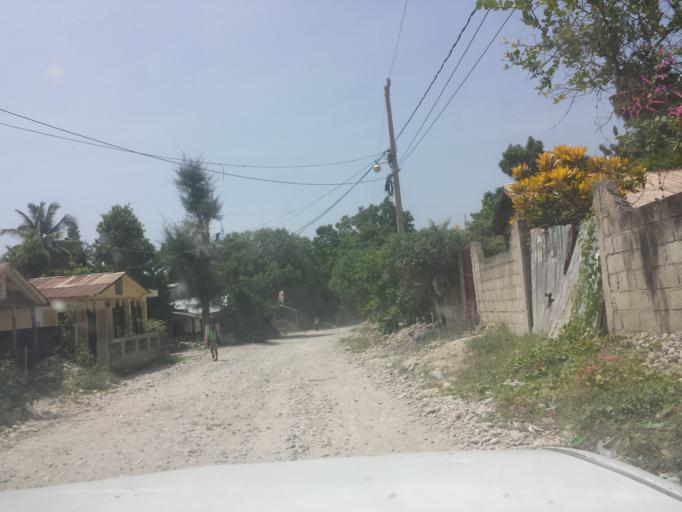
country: HT
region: Sud-Est
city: Marigot
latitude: 18.2322
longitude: -72.3050
